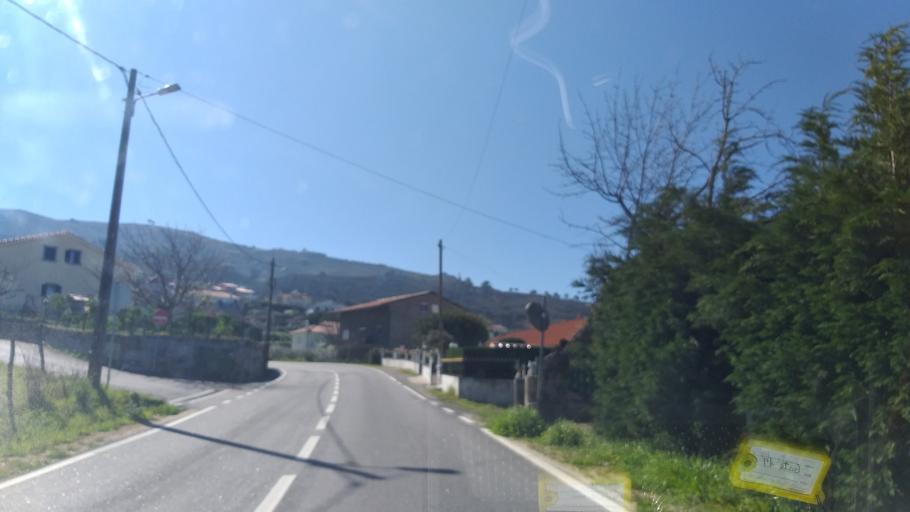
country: PT
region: Guarda
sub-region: Fornos de Algodres
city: Fornos de Algodres
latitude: 40.5232
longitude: -7.5522
